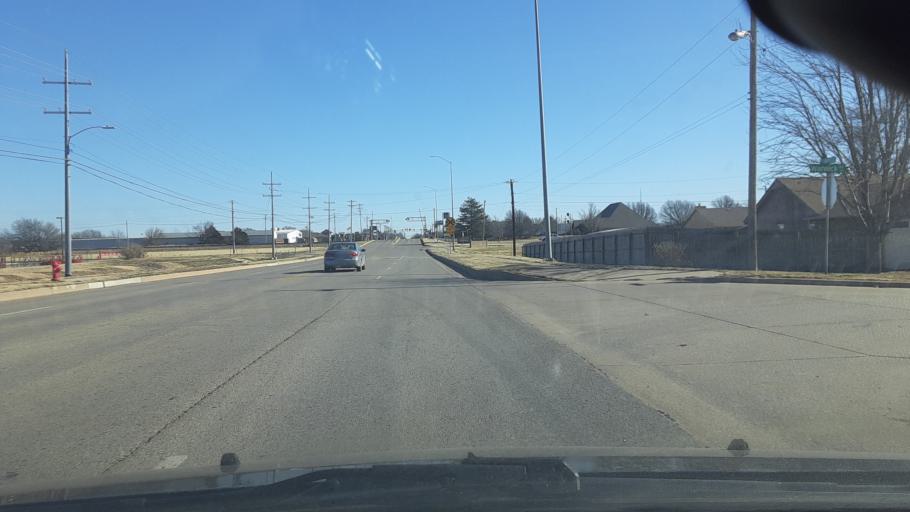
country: US
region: Oklahoma
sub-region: Kay County
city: Ponca City
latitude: 36.7386
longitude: -97.0797
